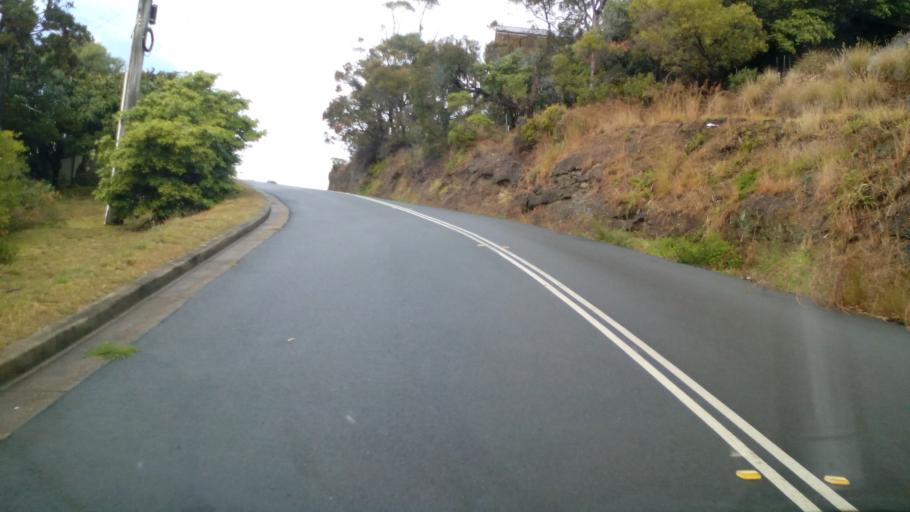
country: AU
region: New South Wales
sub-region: Lake Macquarie Shire
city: Belmont South
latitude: -33.1088
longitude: 151.6401
